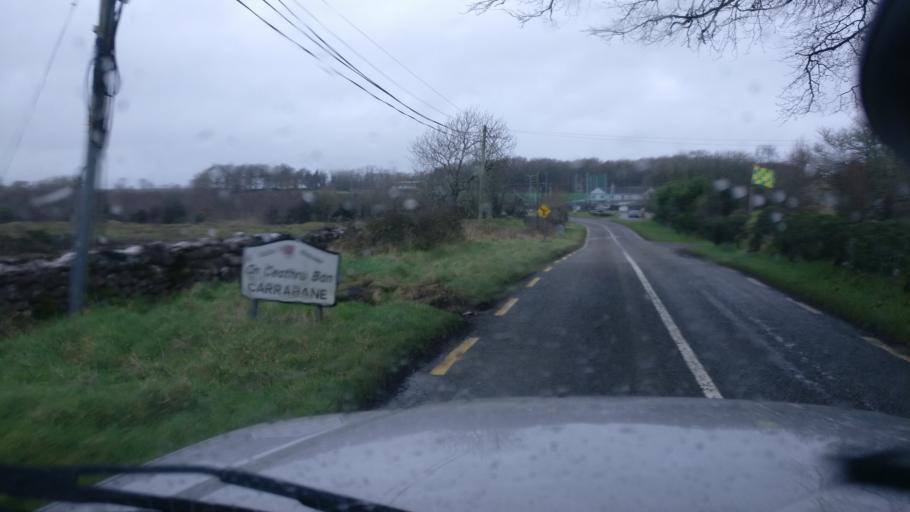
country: IE
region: Connaught
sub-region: County Galway
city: Loughrea
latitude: 53.2253
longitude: -8.6297
